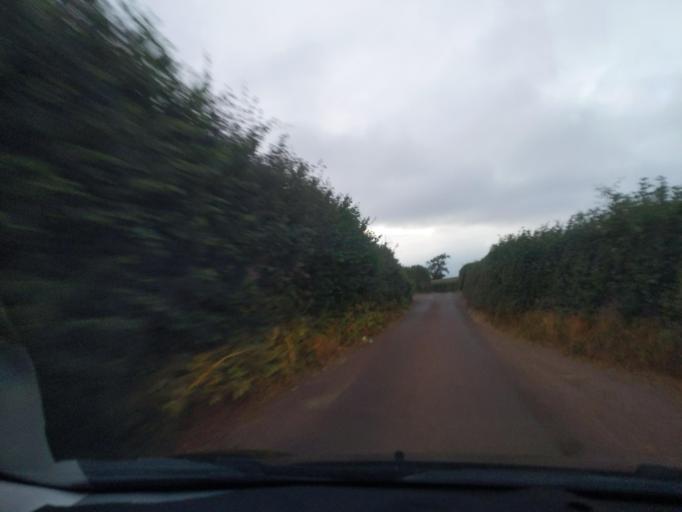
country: GB
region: England
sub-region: Devon
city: Marldon
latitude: 50.4691
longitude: -3.6131
